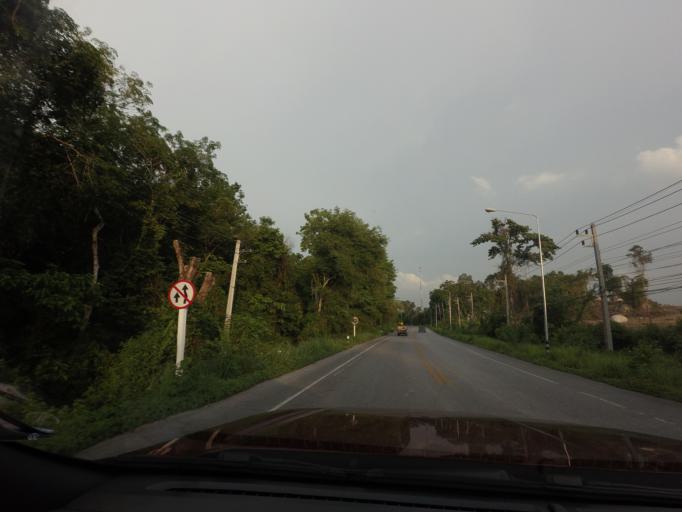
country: TH
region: Pattani
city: Mae Lan
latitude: 6.6698
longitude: 101.1594
